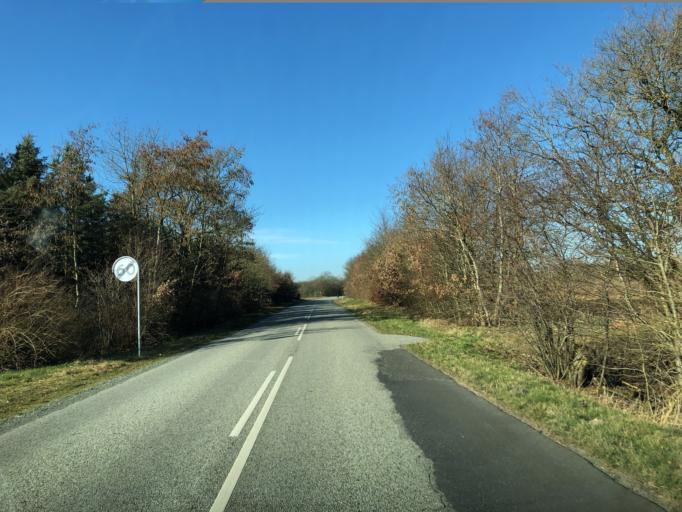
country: DK
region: Central Jutland
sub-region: Ikast-Brande Kommune
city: Bording Kirkeby
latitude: 56.1532
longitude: 9.2658
